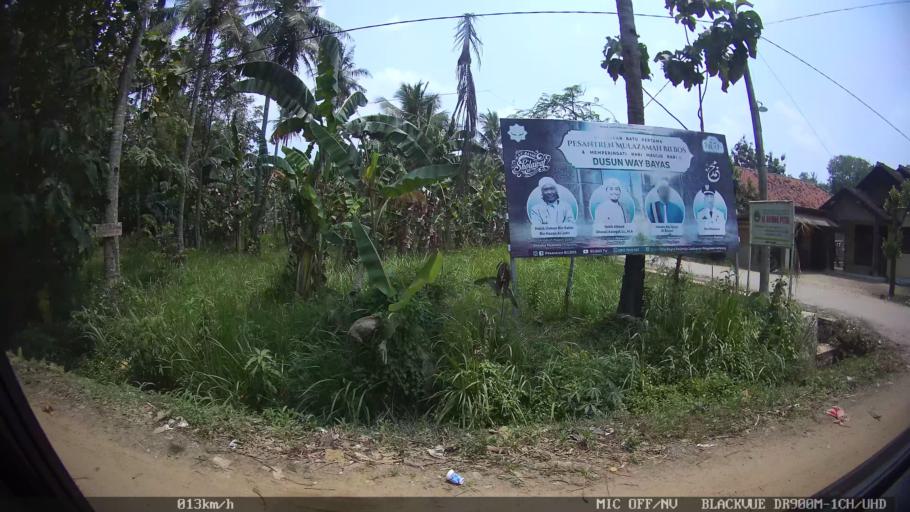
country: ID
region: Lampung
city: Pringsewu
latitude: -5.3829
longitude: 105.0133
